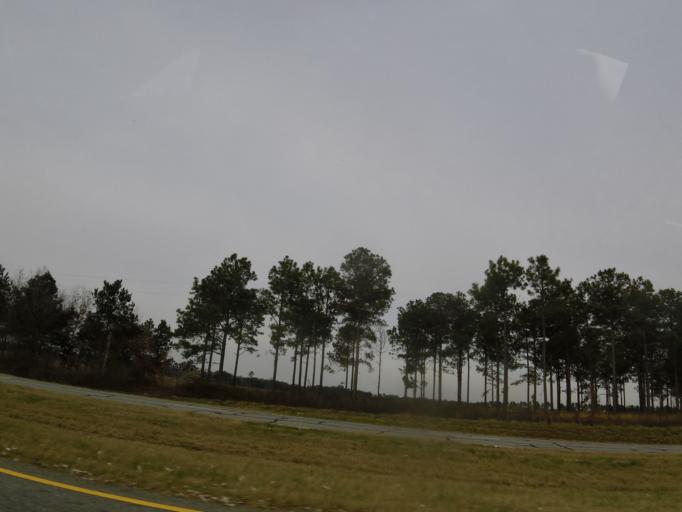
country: US
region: Georgia
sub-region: Decatur County
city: Bainbridge
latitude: 30.9403
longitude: -84.6748
